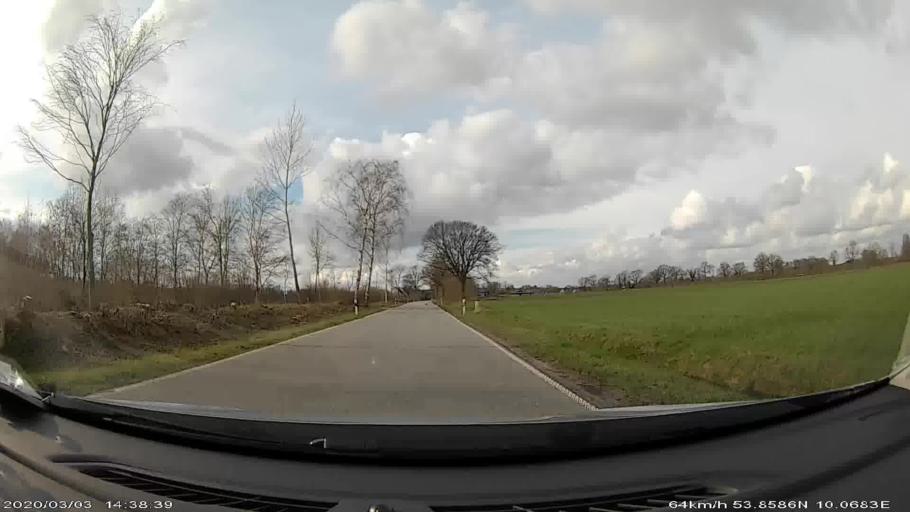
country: DE
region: Schleswig-Holstein
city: Struvenhutten
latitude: 53.8586
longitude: 10.0685
